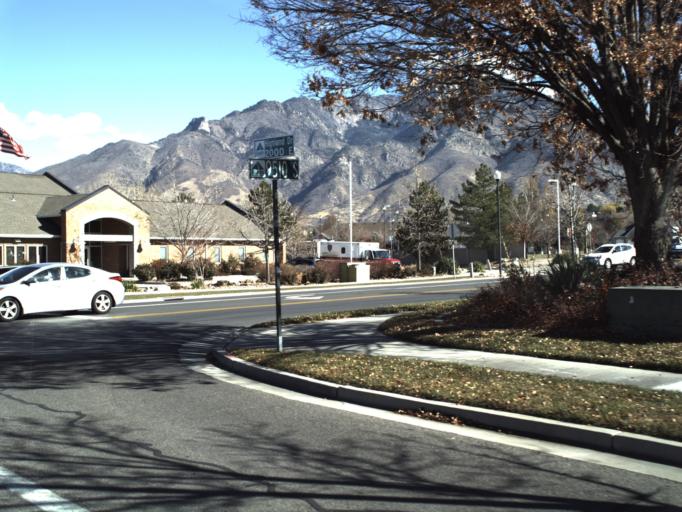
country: US
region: Utah
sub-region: Salt Lake County
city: Sandy Hills
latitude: 40.5785
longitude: -111.8345
